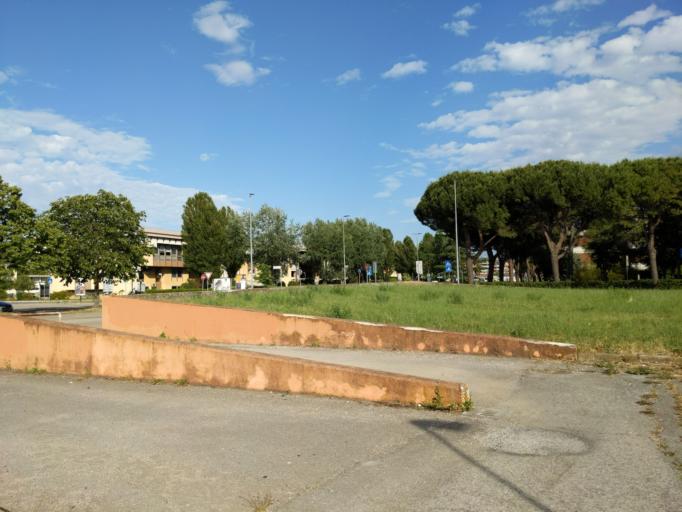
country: IT
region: The Marches
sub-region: Provincia di Pesaro e Urbino
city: Pesaro
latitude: 43.8939
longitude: 12.8954
